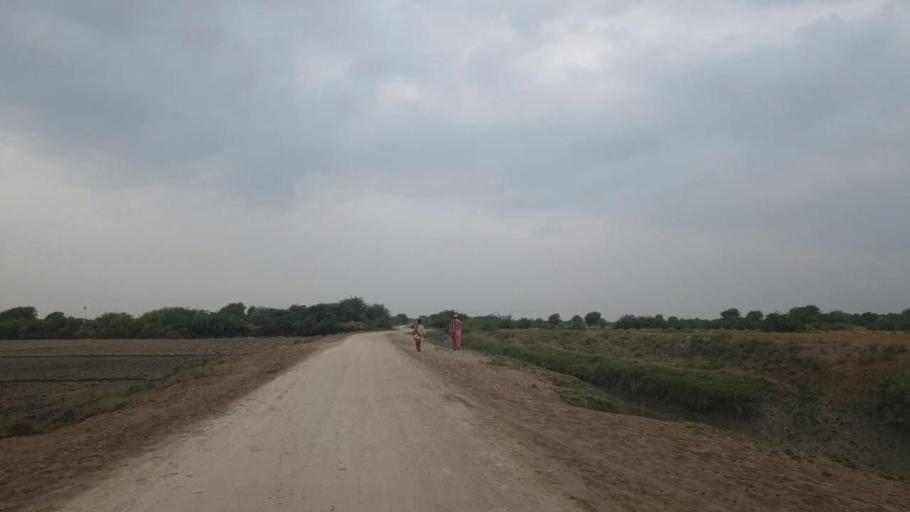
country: PK
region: Sindh
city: Badin
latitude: 24.6425
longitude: 68.6813
